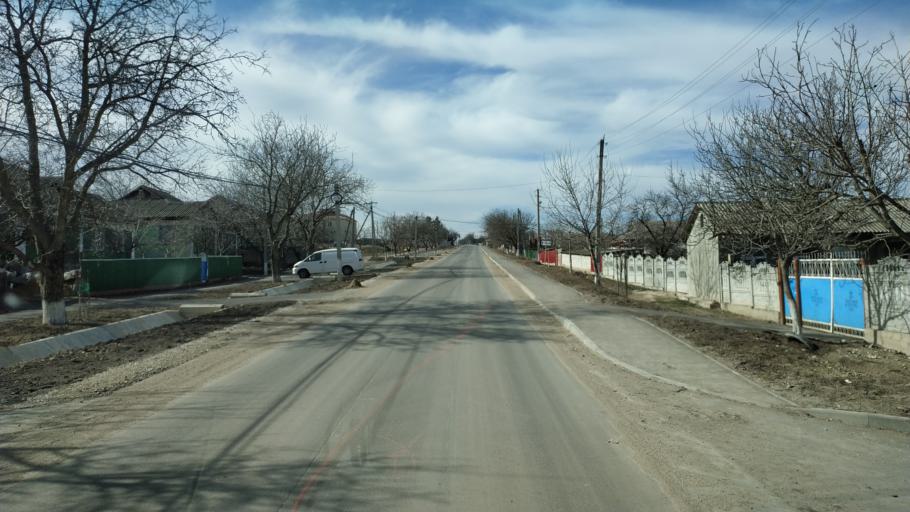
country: RO
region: Iasi
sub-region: Comuna Grozesti
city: Grozesti
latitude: 46.9642
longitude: 28.1651
